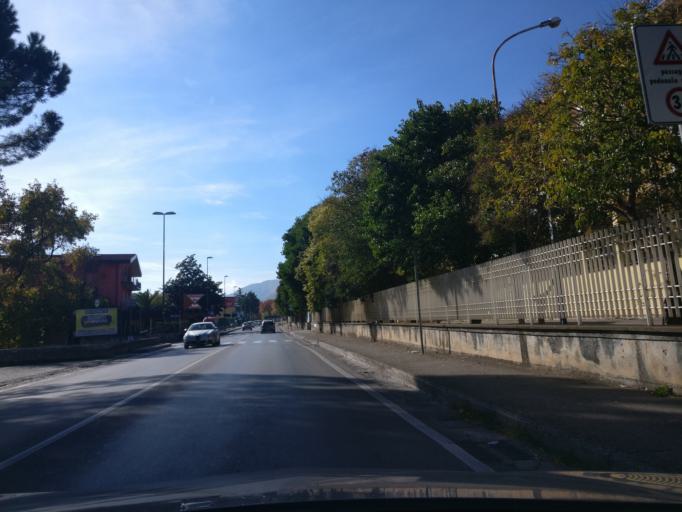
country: IT
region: Campania
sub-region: Provincia di Avellino
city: Avellino
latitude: 40.9203
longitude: 14.7776
